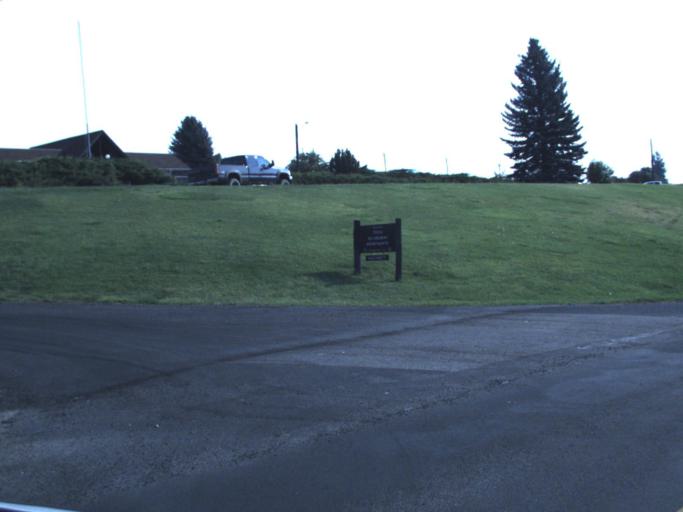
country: US
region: Idaho
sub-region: Benewah County
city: Plummer
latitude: 47.2293
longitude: -117.0832
